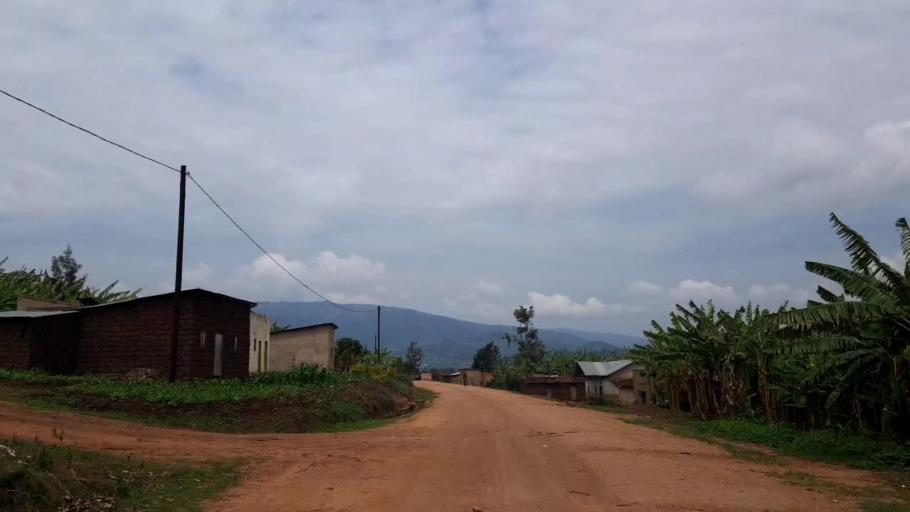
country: RW
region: Northern Province
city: Byumba
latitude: -1.4977
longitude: 30.2260
